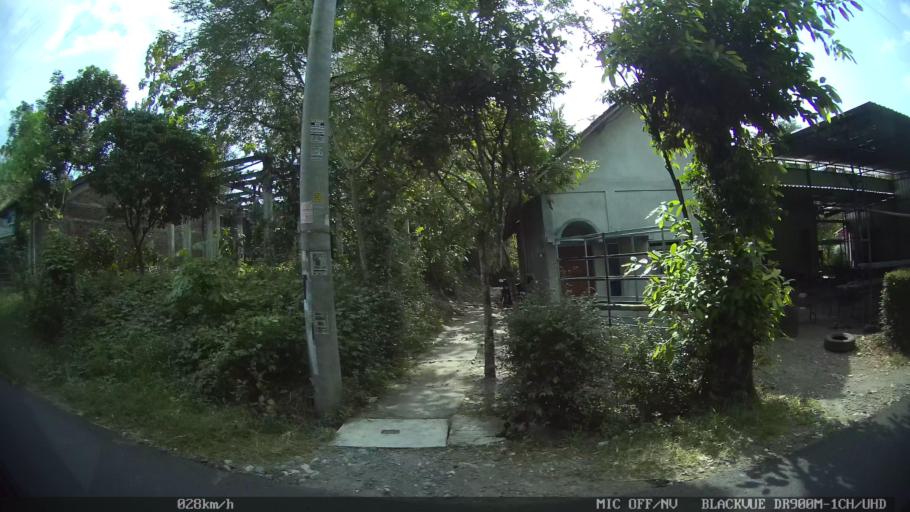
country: ID
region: Daerah Istimewa Yogyakarta
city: Kasihan
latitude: -7.8515
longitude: 110.3138
